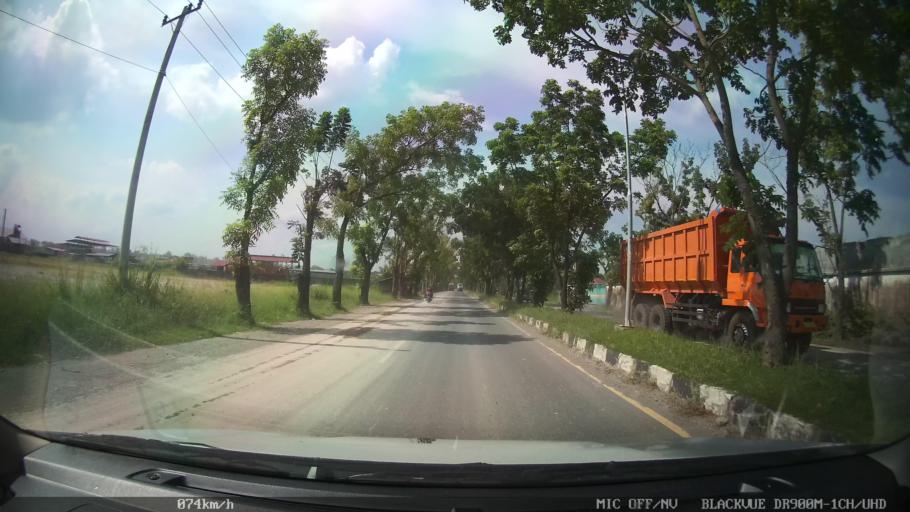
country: ID
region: North Sumatra
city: Binjai
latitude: 3.6304
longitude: 98.5350
